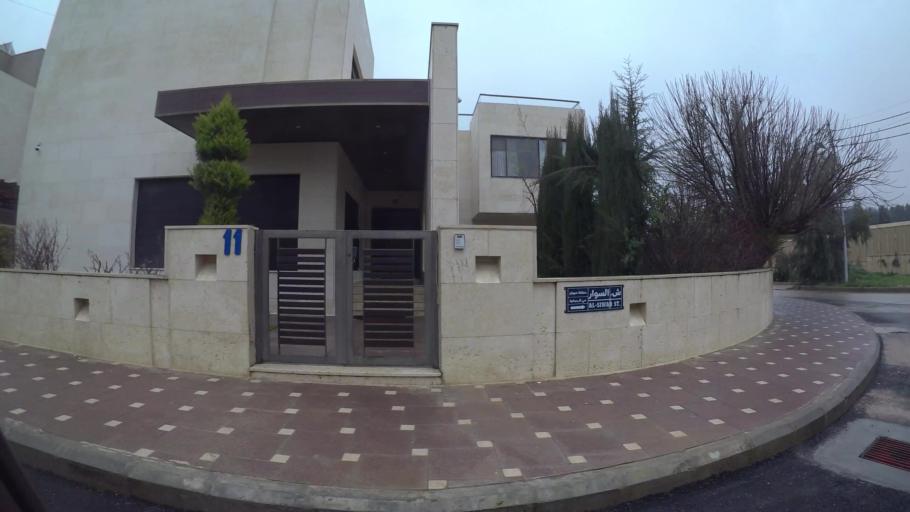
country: JO
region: Amman
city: Al Jubayhah
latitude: 32.0038
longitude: 35.8186
